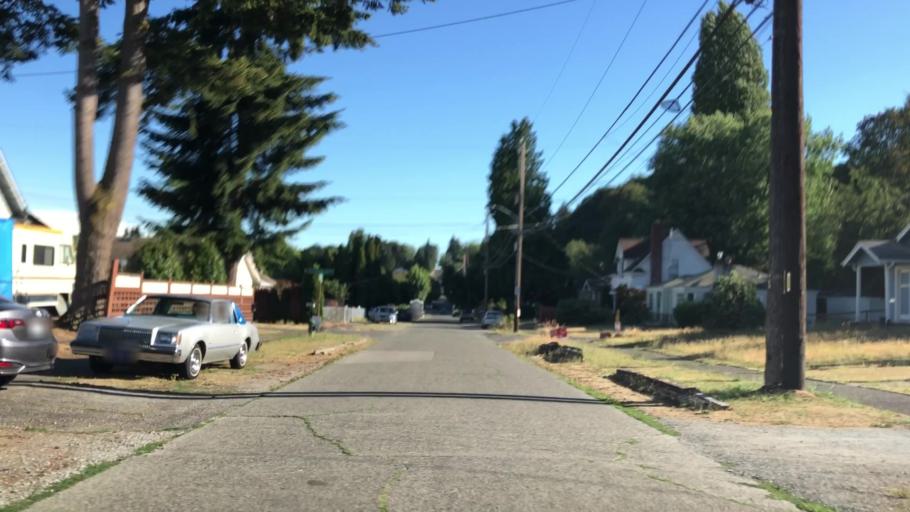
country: US
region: Washington
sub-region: King County
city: Seattle
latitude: 47.5530
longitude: -122.2916
